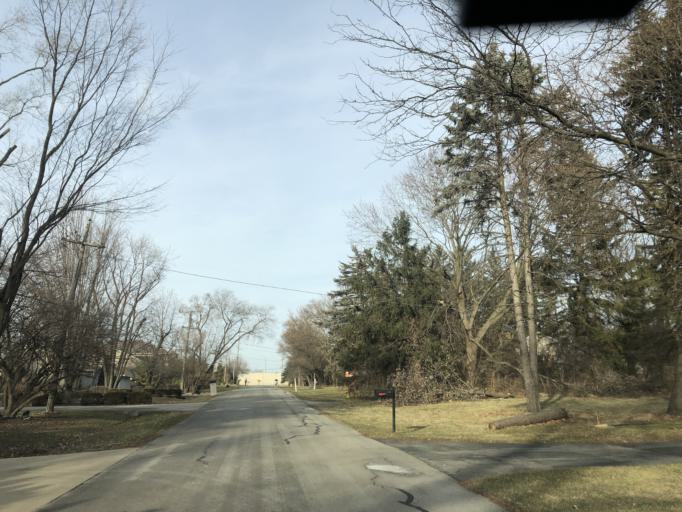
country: US
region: Illinois
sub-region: Cook County
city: Lemont
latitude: 41.7124
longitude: -88.0099
